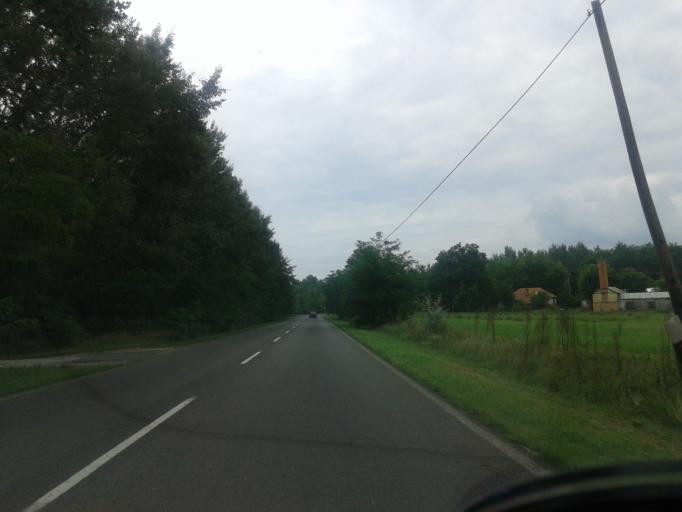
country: HU
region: Csongrad
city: Ruzsa
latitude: 46.2495
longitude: 19.6838
